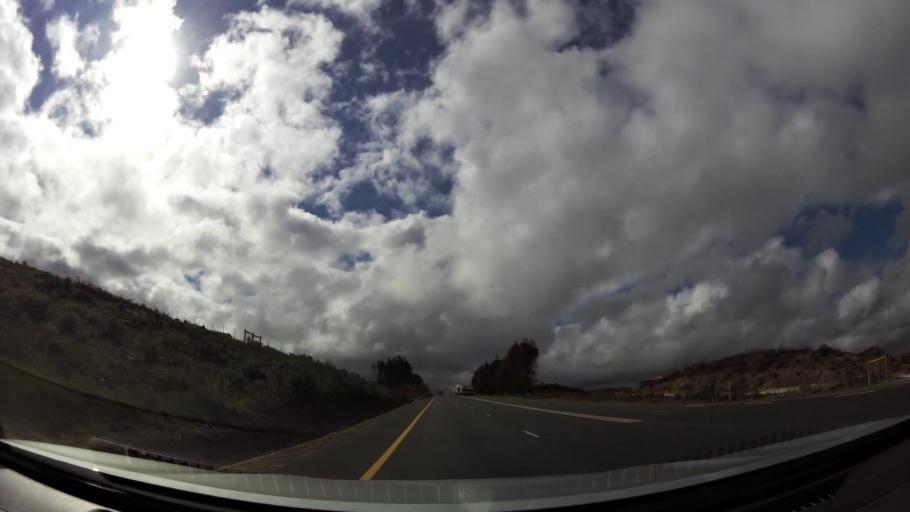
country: ZA
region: Western Cape
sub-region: Eden District Municipality
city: Knysna
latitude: -34.0390
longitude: 23.1206
